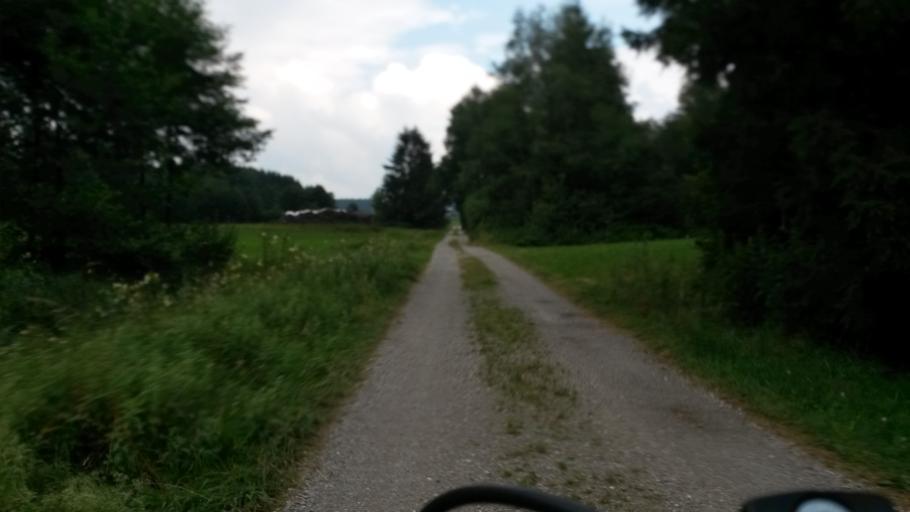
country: DE
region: Bavaria
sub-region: Upper Bavaria
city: Hoslwang
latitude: 47.9382
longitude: 12.3298
